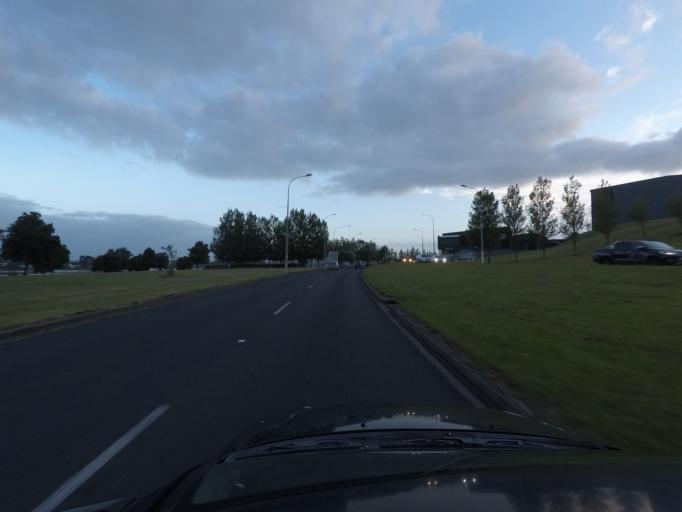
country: NZ
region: Auckland
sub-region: Auckland
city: Tamaki
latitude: -36.9418
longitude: 174.8629
